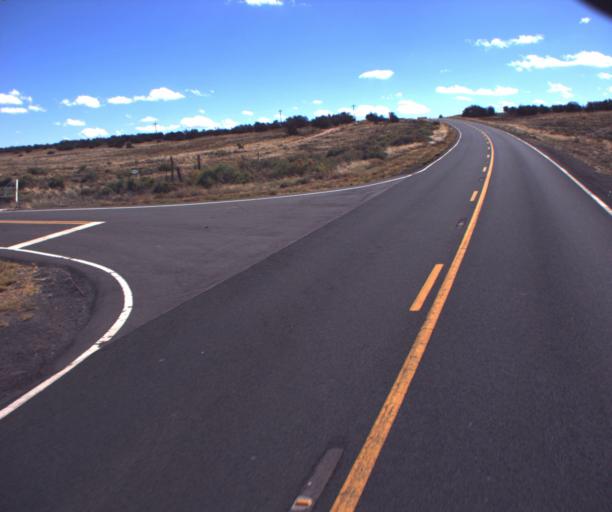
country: US
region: Arizona
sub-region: Apache County
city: Houck
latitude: 35.0849
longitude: -109.3088
